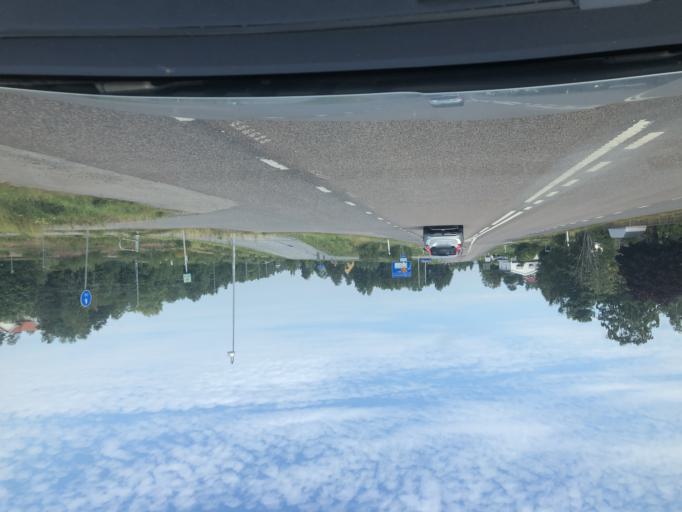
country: SE
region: Vaesternorrland
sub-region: Kramfors Kommun
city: Kramfors
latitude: 62.9027
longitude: 17.8324
